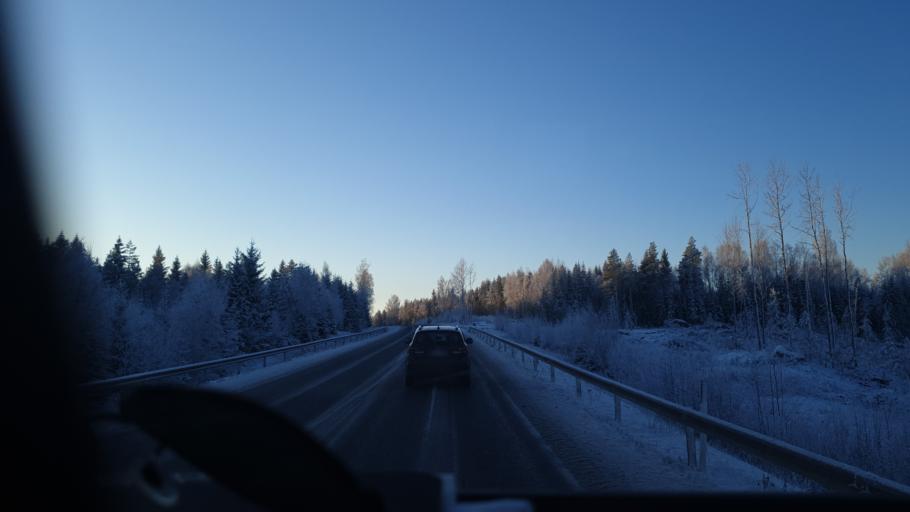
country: FI
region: Central Ostrobothnia
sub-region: Kokkola
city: Kaelviae
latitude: 63.9083
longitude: 23.3895
